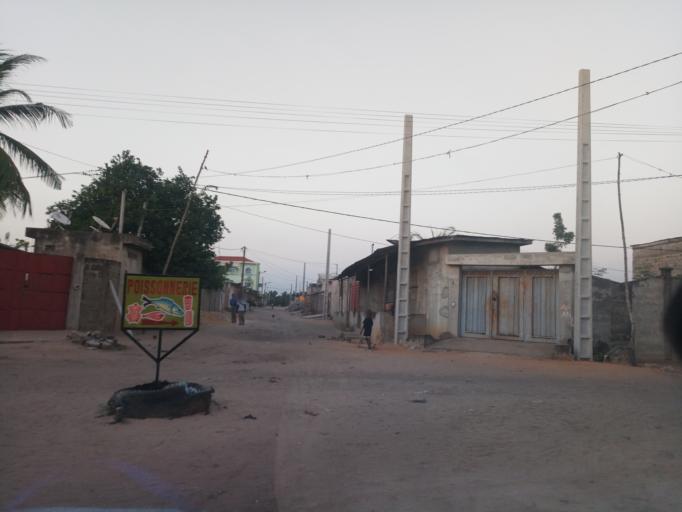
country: BJ
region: Atlantique
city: Hevie
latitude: 6.3927
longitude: 2.2881
